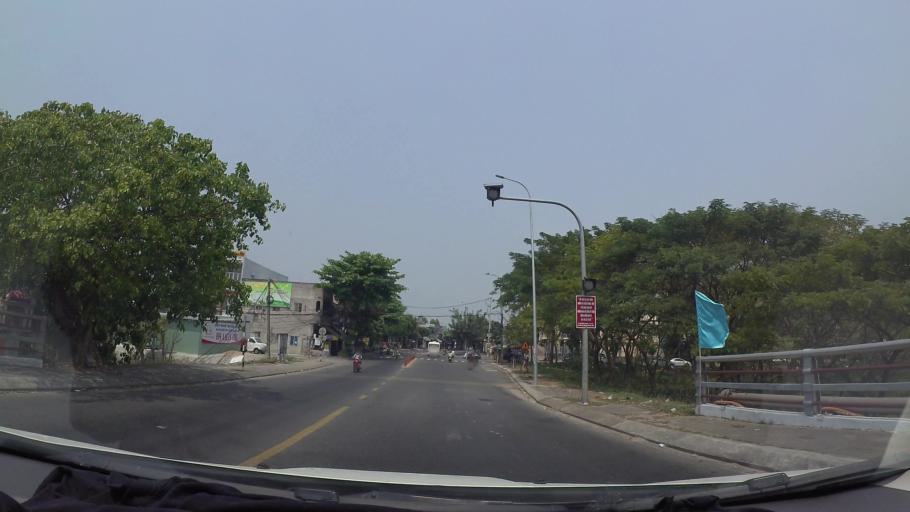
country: VN
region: Da Nang
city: Cam Le
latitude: 16.0109
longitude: 108.2060
